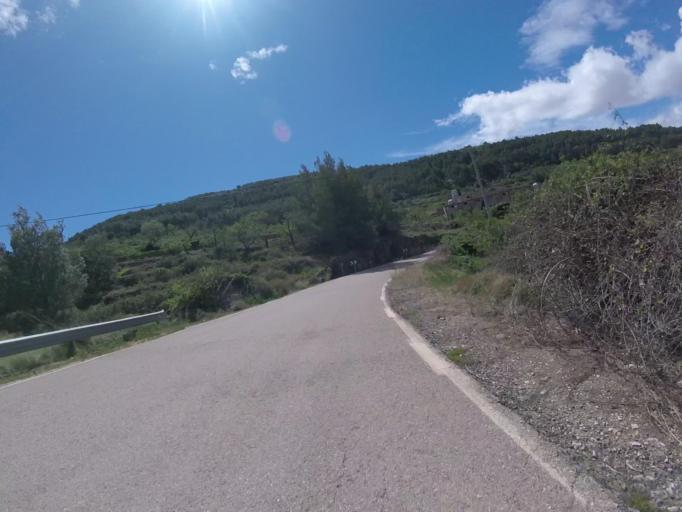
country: ES
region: Valencia
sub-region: Provincia de Castello
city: Sierra-Engarceran
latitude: 40.2726
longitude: -0.0118
